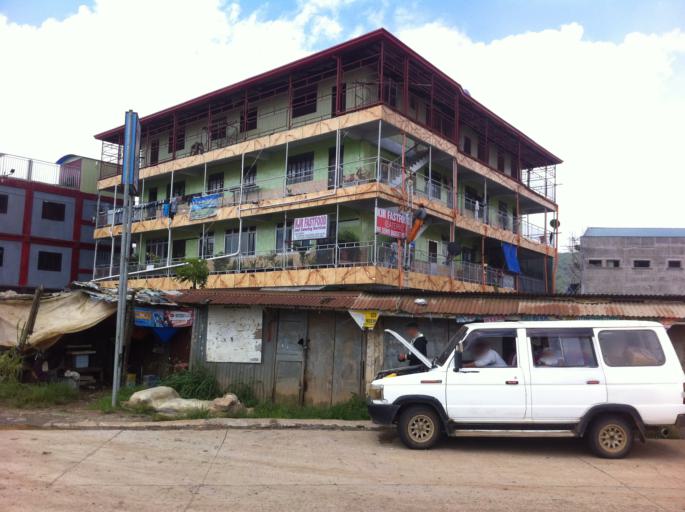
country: PH
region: Cordillera
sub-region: Province of Benguet
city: La Trinidad
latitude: 16.4534
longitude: 120.5805
